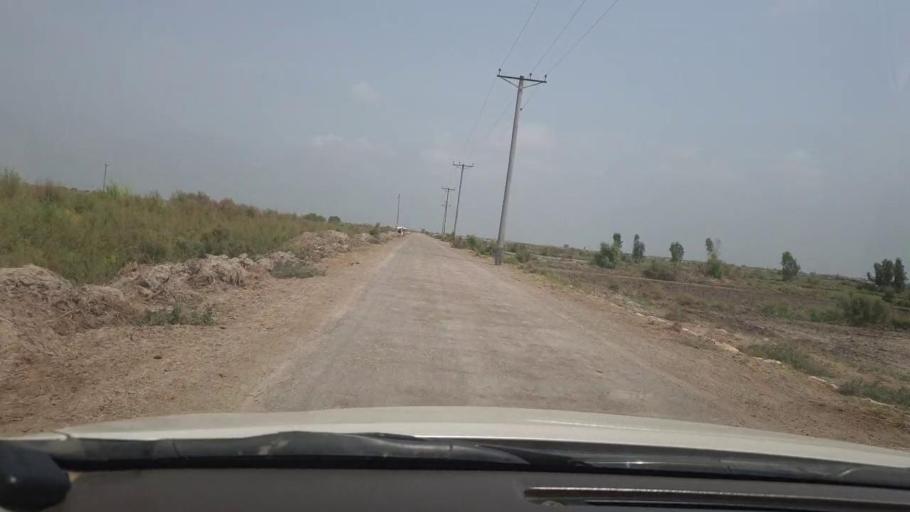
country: PK
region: Sindh
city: Garhi Yasin
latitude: 28.0058
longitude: 68.4998
